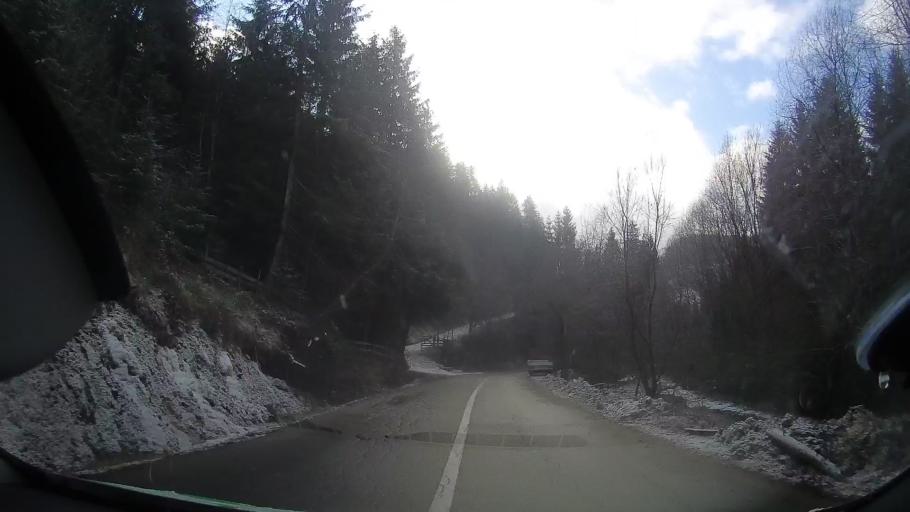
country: RO
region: Alba
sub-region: Comuna Horea
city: Horea
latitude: 46.4842
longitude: 22.9621
